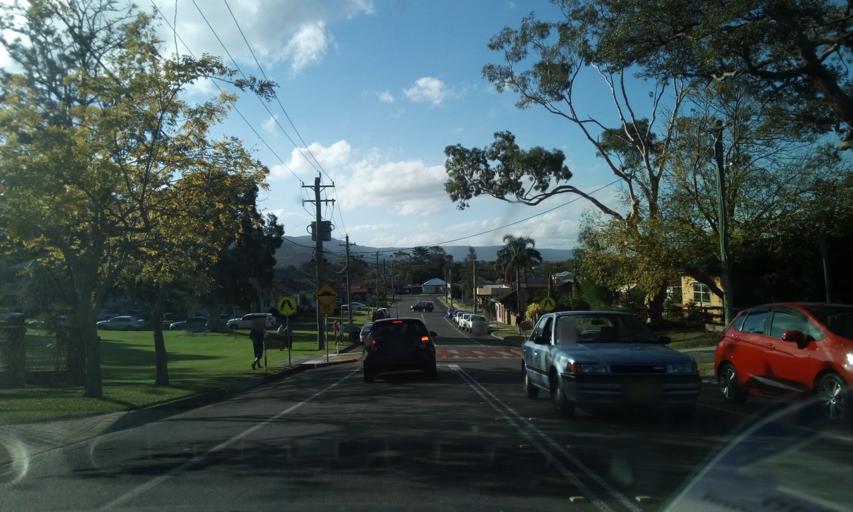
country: AU
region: New South Wales
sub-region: Wollongong
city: Fairy Meadow
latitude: -34.3989
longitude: 150.8868
